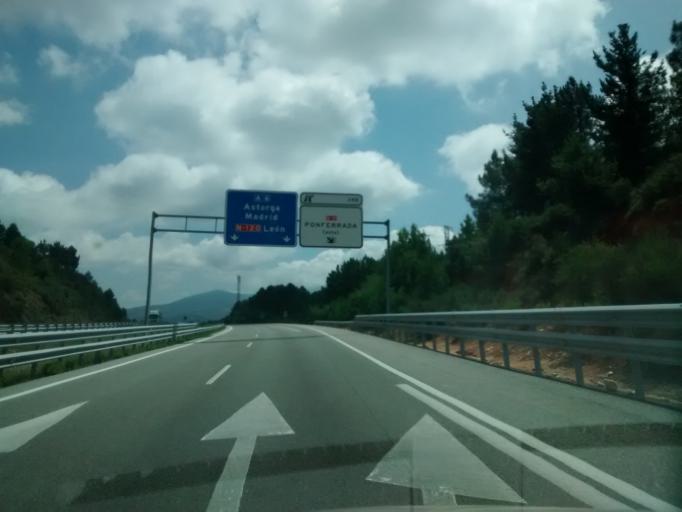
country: ES
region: Castille and Leon
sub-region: Provincia de Leon
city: Ponferrada
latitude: 42.5606
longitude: -6.5624
